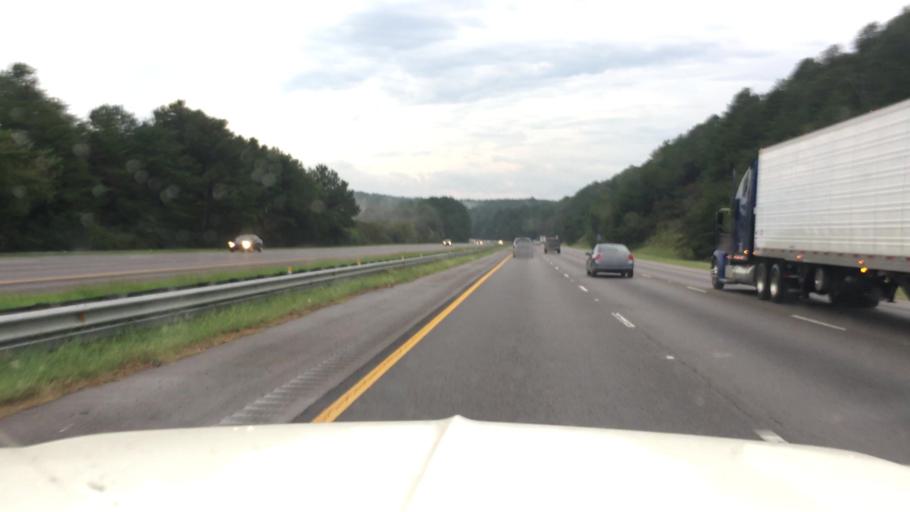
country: US
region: Alabama
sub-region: Jefferson County
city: Morris
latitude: 33.7132
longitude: -86.8324
